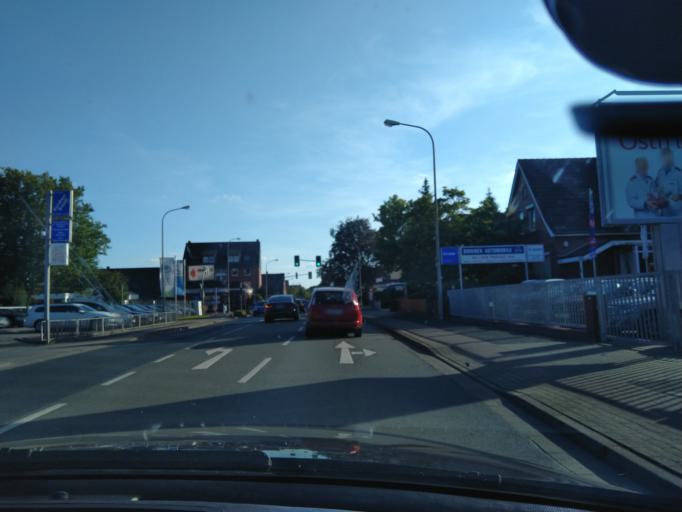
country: DE
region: Lower Saxony
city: Leer
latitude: 53.2445
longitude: 7.4572
